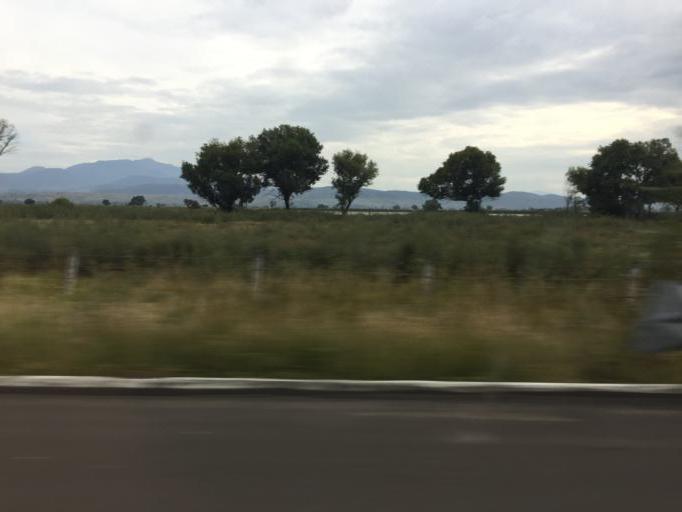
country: MX
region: Mexico
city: Huaniqueo de Morales
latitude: 19.8914
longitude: -101.5327
